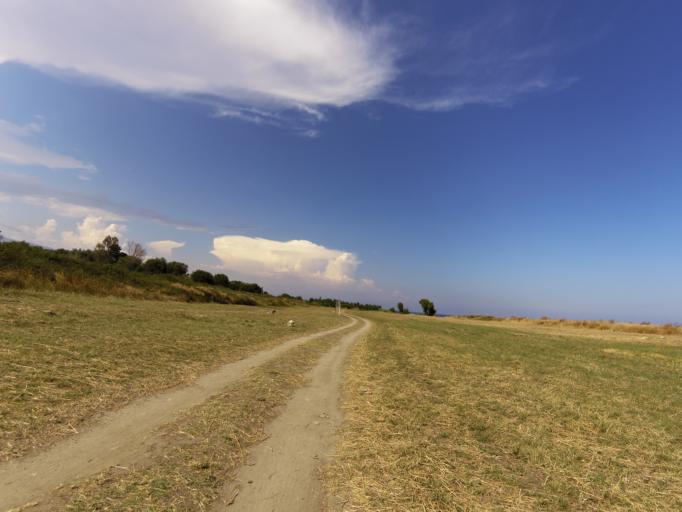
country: IT
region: Calabria
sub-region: Provincia di Reggio Calabria
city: Monasterace Marina
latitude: 38.4474
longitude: 16.5792
